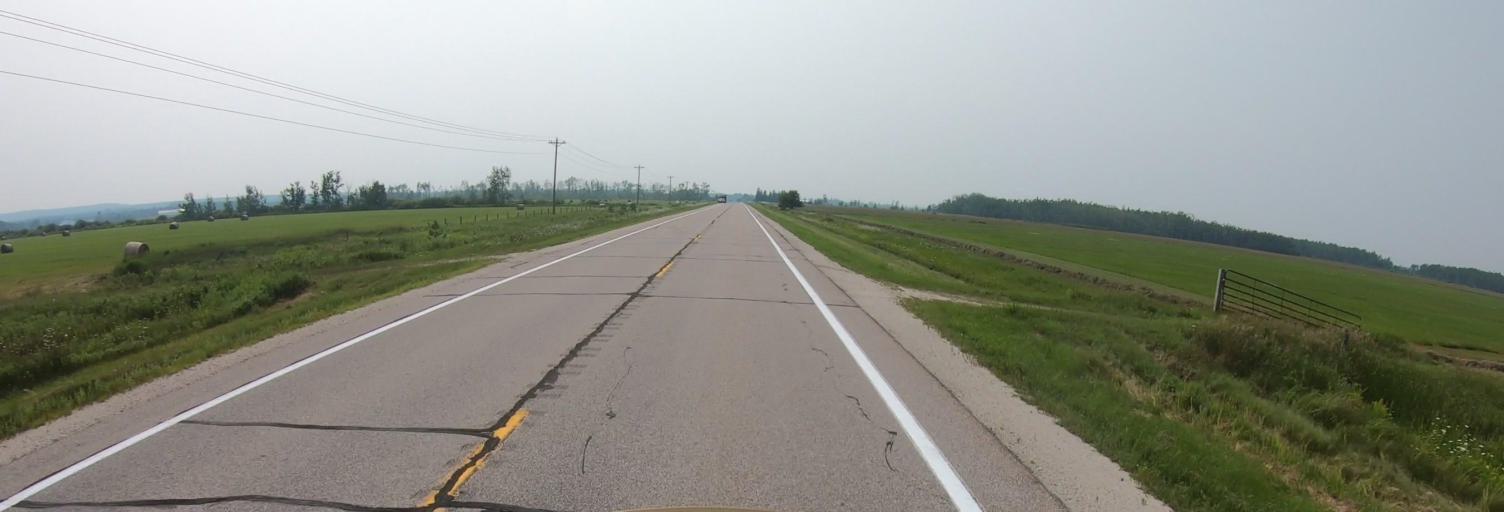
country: US
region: Michigan
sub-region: Chippewa County
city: Sault Ste. Marie
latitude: 46.1290
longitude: -84.3088
